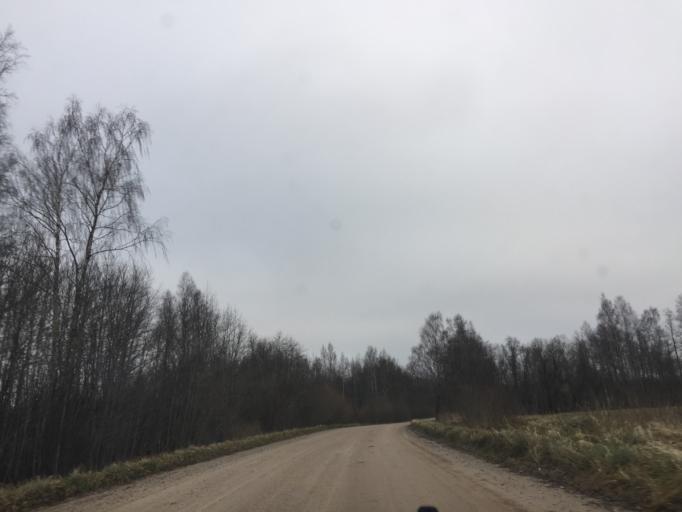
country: LV
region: Limbazu Rajons
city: Limbazi
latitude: 57.5877
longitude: 24.5137
